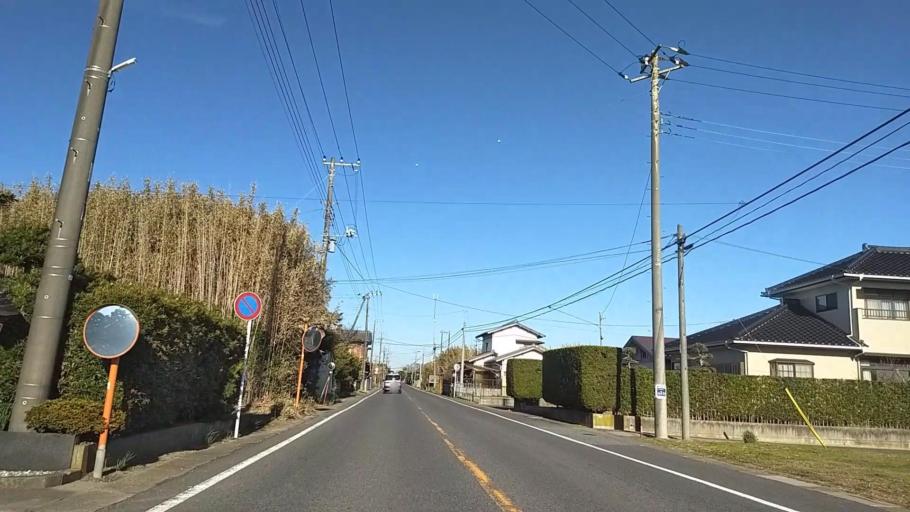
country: JP
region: Chiba
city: Naruto
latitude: 35.5757
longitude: 140.4871
